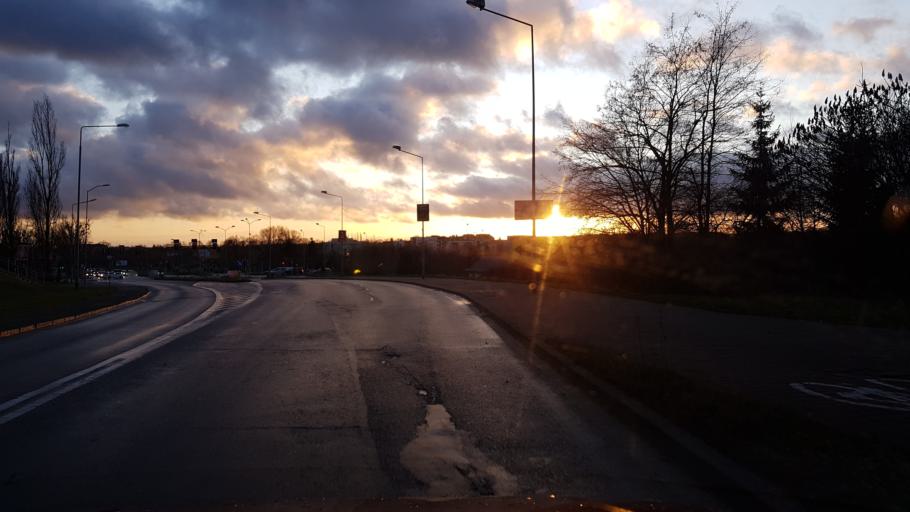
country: PL
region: West Pomeranian Voivodeship
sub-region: Szczecin
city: Szczecin
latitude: 53.4304
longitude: 14.5008
